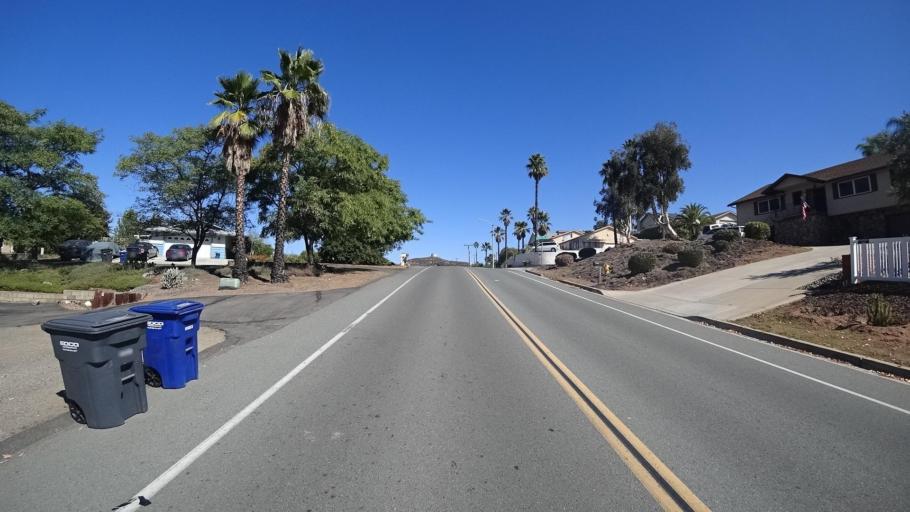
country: US
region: California
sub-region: San Diego County
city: Winter Gardens
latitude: 32.8215
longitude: -116.9217
